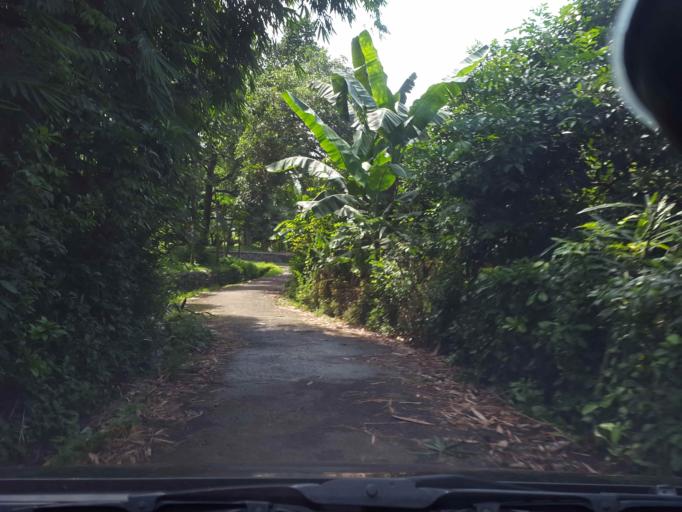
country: ID
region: West Nusa Tenggara
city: Jejelok
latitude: -8.6054
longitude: 116.1696
